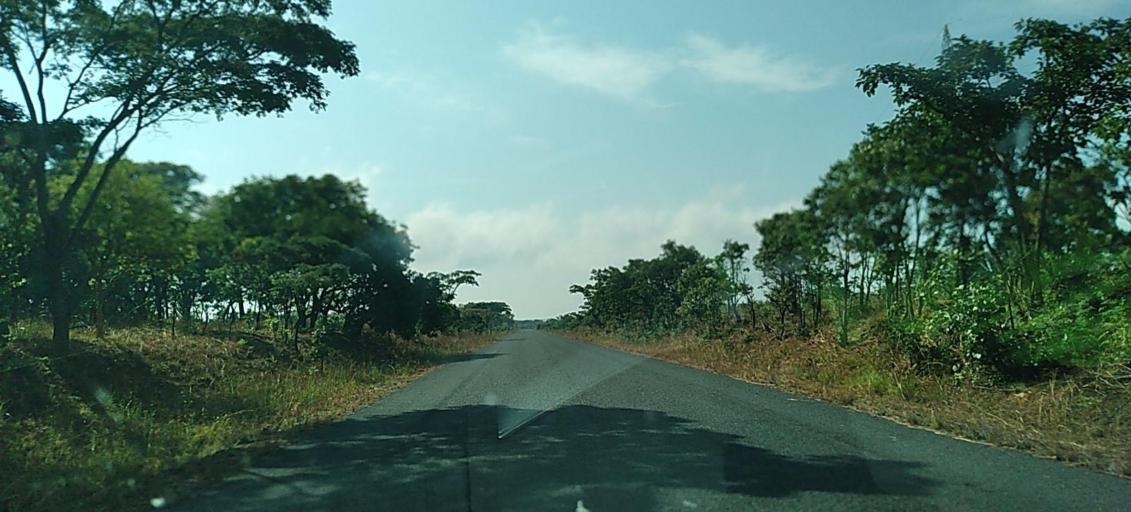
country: ZM
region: North-Western
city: Mwinilunga
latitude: -11.7405
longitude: 24.9846
